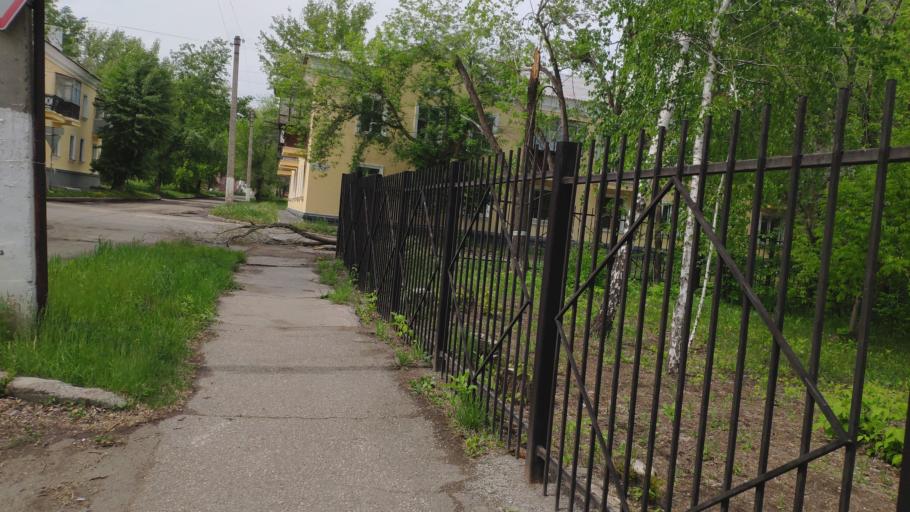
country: RU
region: Chelyabinsk
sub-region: Gorod Magnitogorsk
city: Magnitogorsk
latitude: 53.4193
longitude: 58.9556
